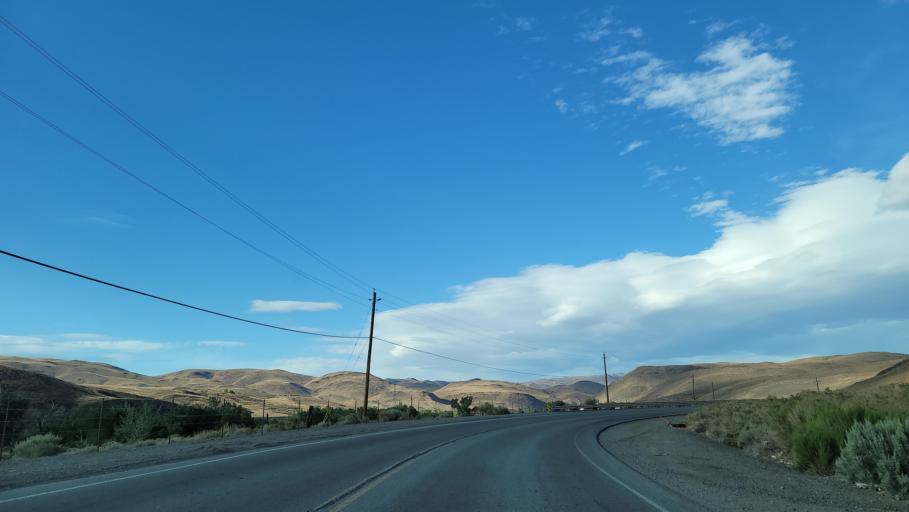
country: US
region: Nevada
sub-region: Washoe County
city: Sparks
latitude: 39.5197
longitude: -119.6117
